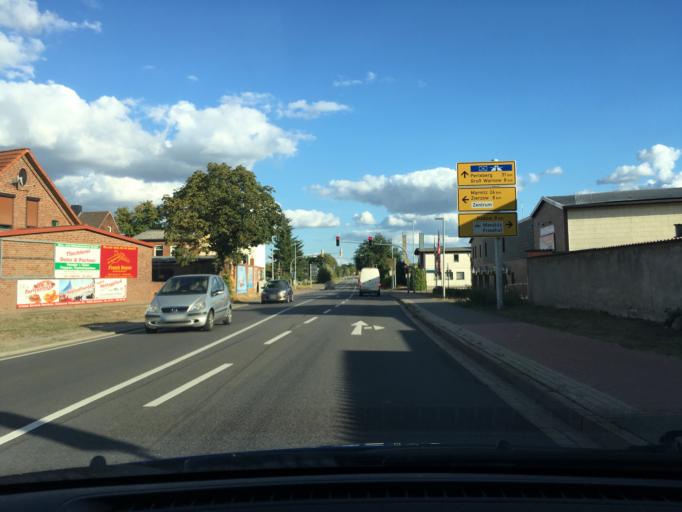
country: DE
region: Mecklenburg-Vorpommern
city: Grabow
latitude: 53.2751
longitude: 11.5590
